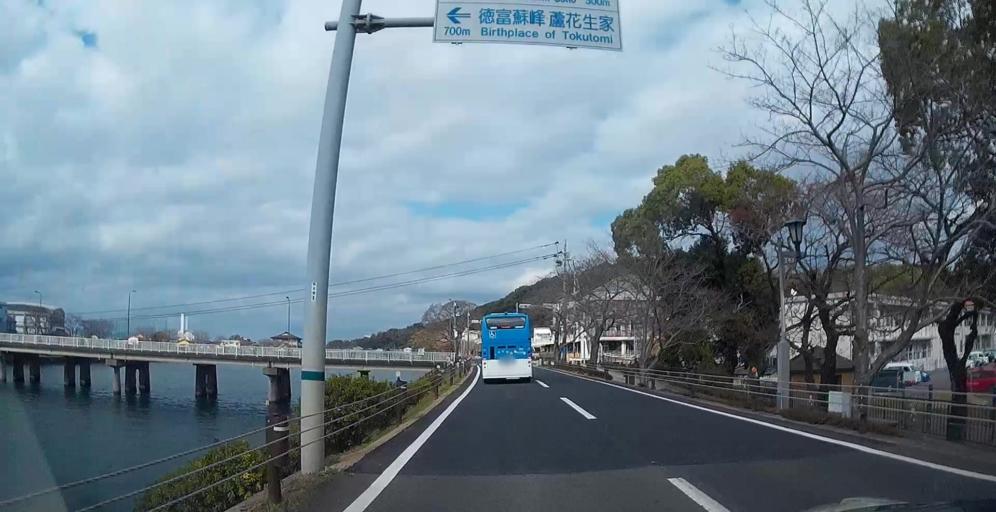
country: JP
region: Kumamoto
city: Minamata
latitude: 32.2138
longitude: 130.4067
